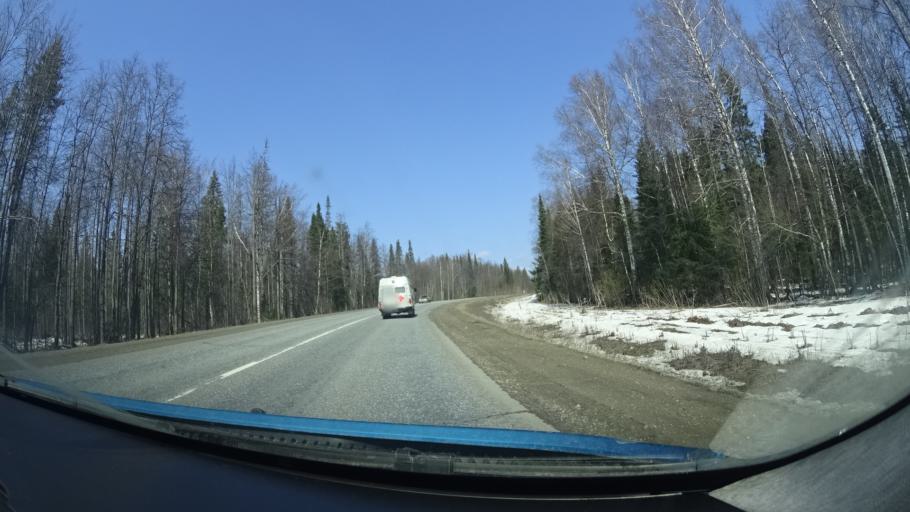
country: RU
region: Perm
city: Yugo-Kamskiy
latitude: 57.5996
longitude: 55.6529
